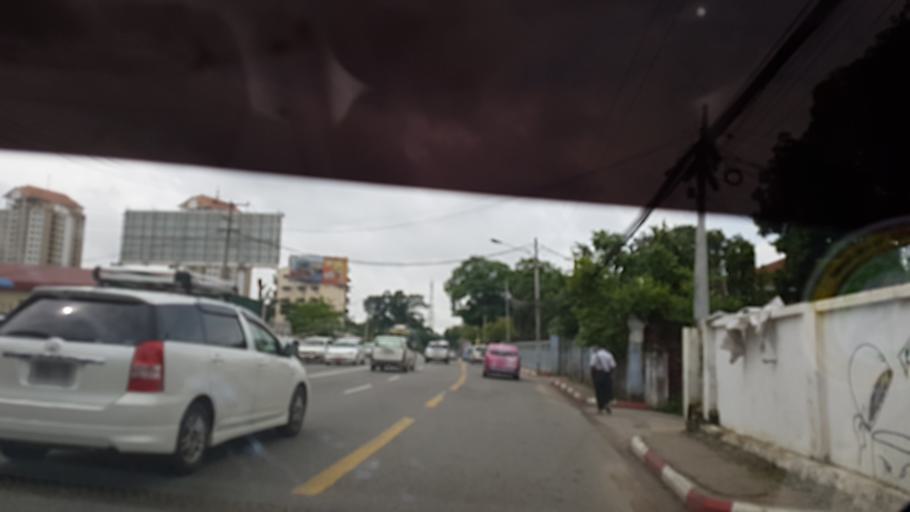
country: MM
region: Yangon
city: Yangon
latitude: 16.8128
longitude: 96.1558
